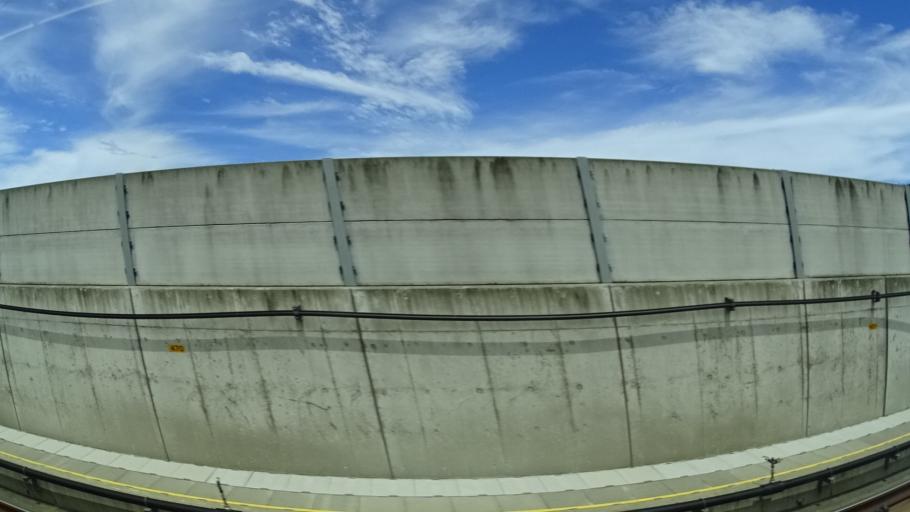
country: JP
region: Niigata
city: Itoigawa
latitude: 37.0851
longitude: 137.9995
